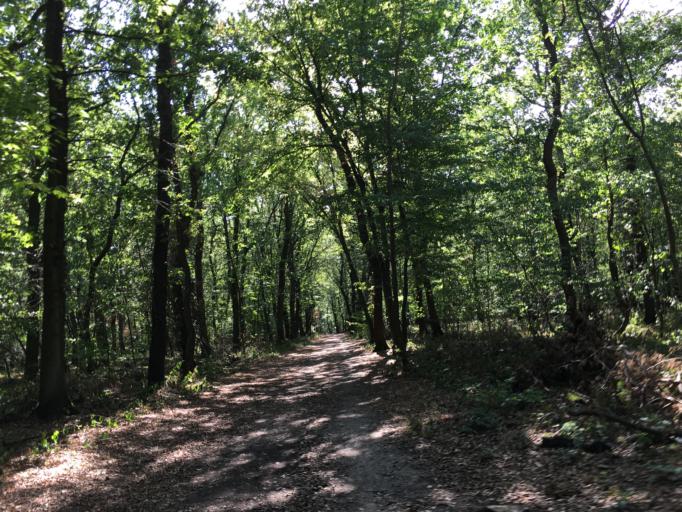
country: DE
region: North Rhine-Westphalia
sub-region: Regierungsbezirk Koln
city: Dueren
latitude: 50.7809
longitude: 6.5012
